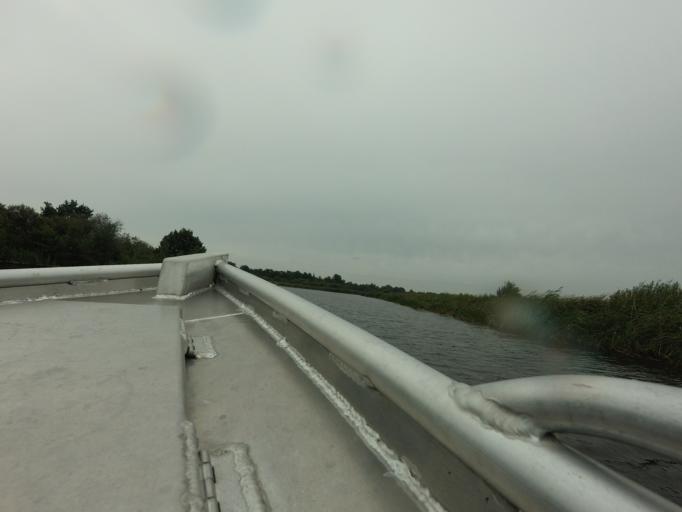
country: NL
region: Overijssel
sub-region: Gemeente Steenwijkerland
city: Sint Jansklooster
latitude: 52.7140
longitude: 6.0170
